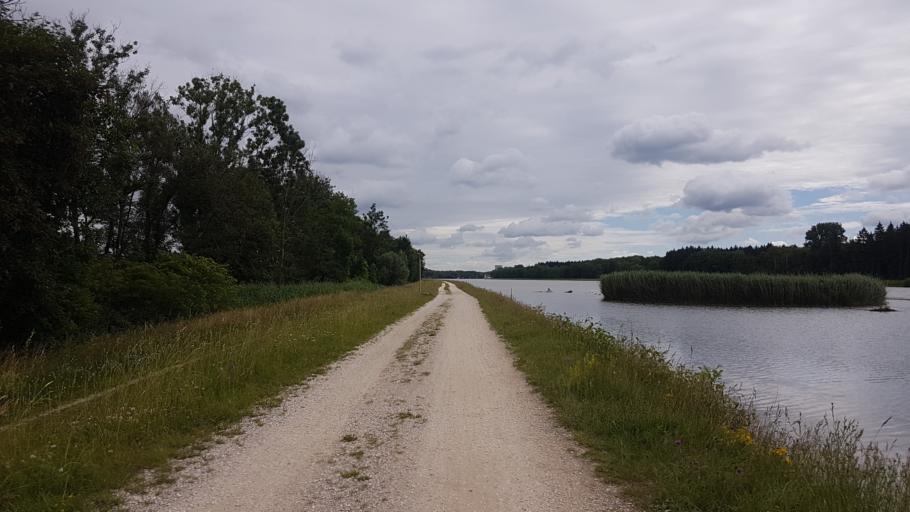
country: DE
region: Bavaria
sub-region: Swabia
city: Rettenbach
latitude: 48.4737
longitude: 10.3164
